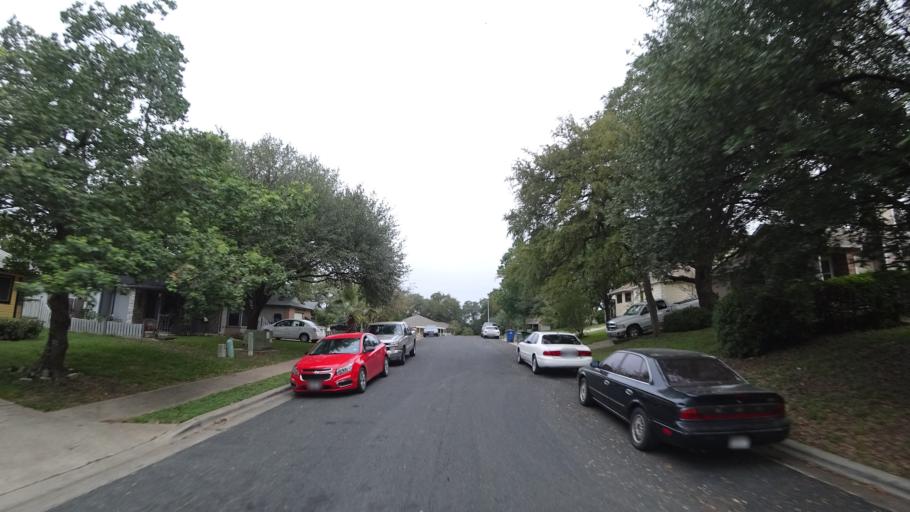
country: US
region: Texas
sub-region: Travis County
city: Austin
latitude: 30.2683
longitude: -97.7108
